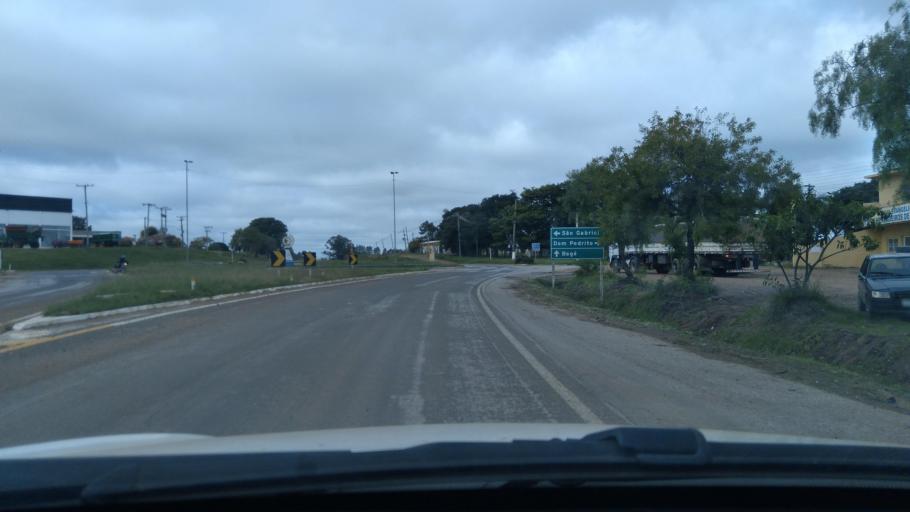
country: BR
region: Rio Grande do Sul
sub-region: Dom Pedrito
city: Dom Pedrito
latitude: -30.9675
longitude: -54.6639
